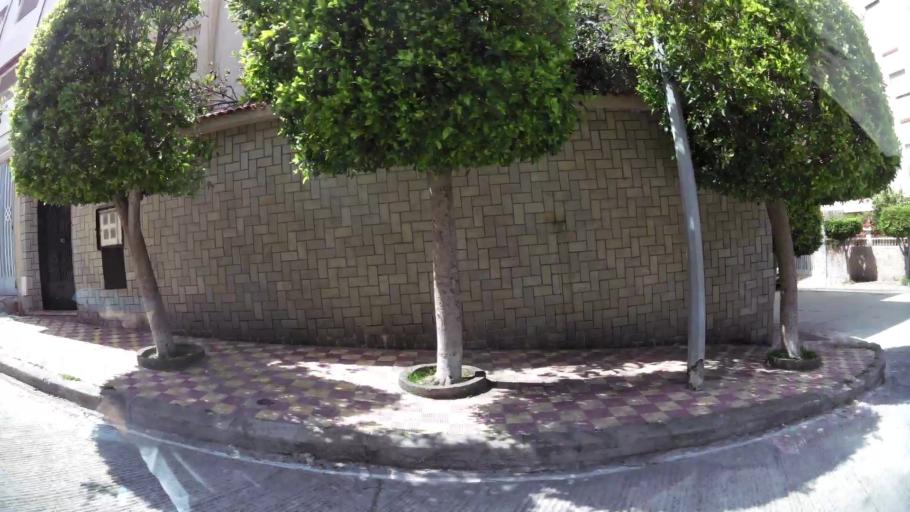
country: MA
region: Tanger-Tetouan
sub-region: Tanger-Assilah
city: Tangier
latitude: 35.7584
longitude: -5.8325
